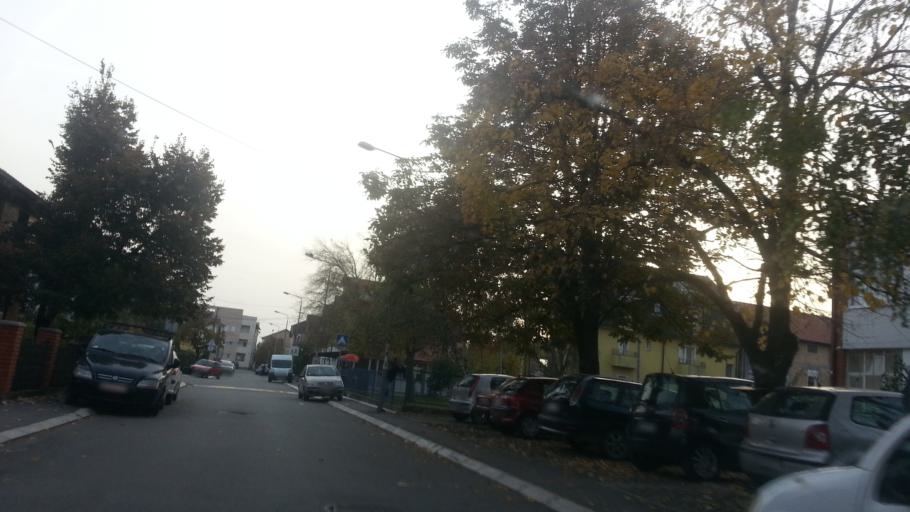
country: RS
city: Novi Banovci
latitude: 44.9002
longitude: 20.2821
